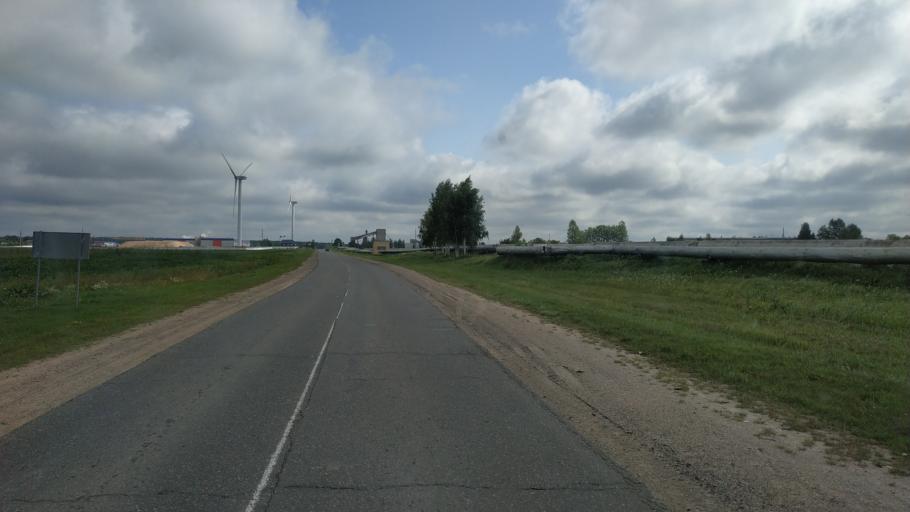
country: BY
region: Mogilev
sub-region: Mahilyowski Rayon
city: Veyno
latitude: 53.8359
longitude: 30.3688
